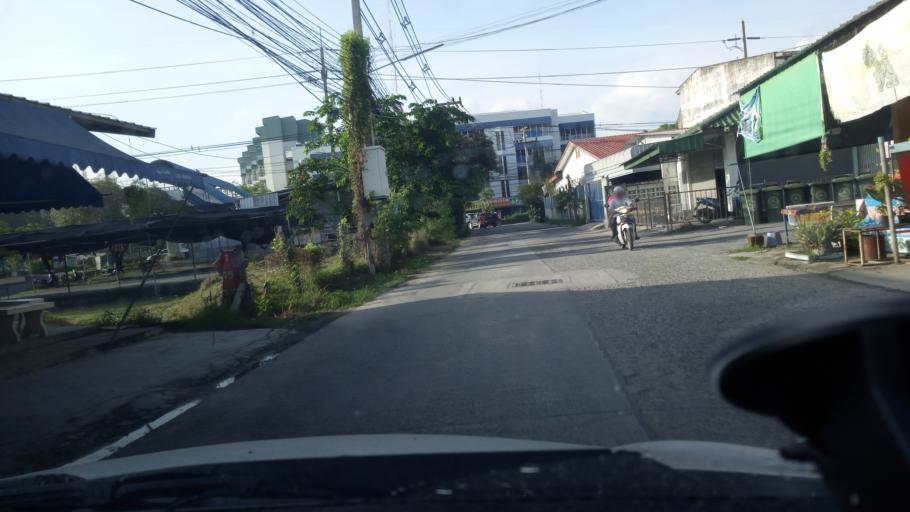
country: TH
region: Chon Buri
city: Phan Thong
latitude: 13.4148
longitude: 101.0612
